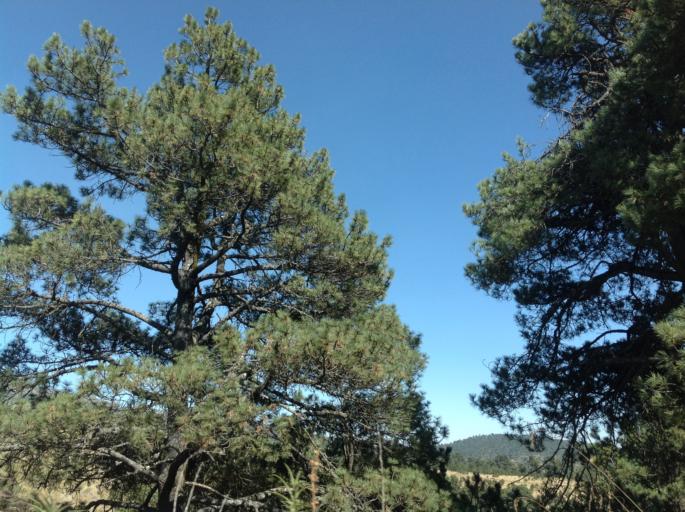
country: MX
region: Mexico
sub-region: Amecameca
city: San Diego Huehuecalco
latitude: 19.1077
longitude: -98.6454
